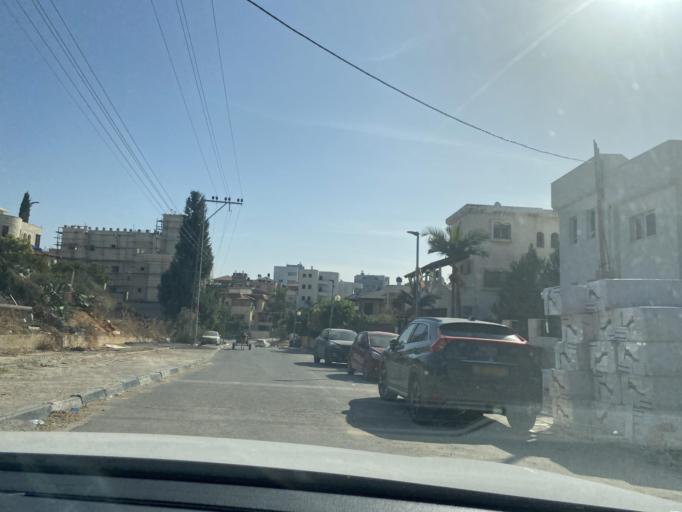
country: IL
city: Oranit
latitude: 32.1321
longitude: 34.9746
